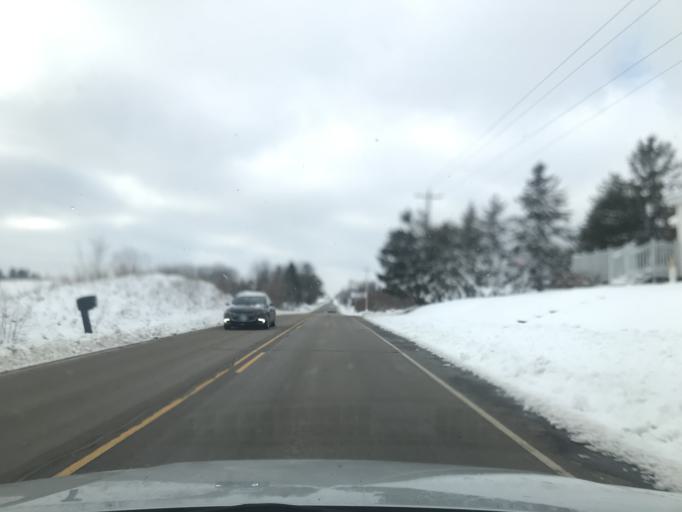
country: US
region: Wisconsin
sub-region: Oconto County
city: Oconto
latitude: 44.9499
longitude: -87.8893
